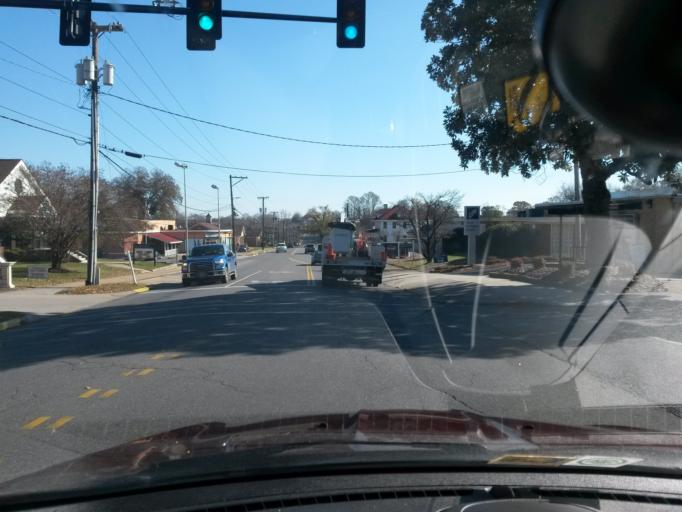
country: US
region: Virginia
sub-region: City of Bedford
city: Bedford
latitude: 37.3338
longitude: -79.5212
